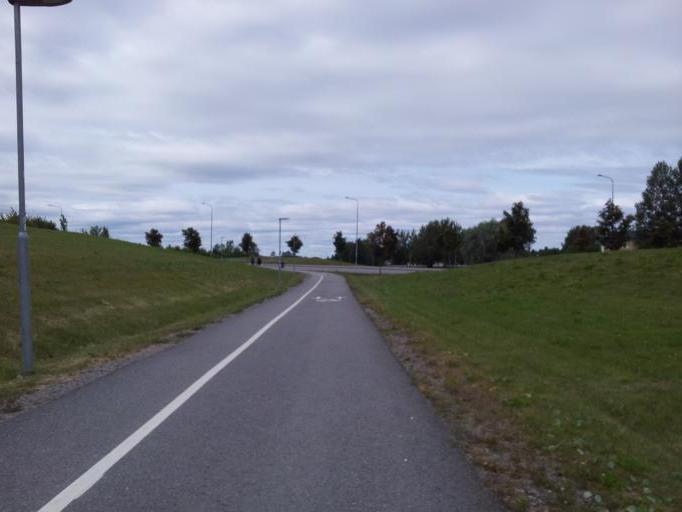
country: SE
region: Uppsala
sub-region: Uppsala Kommun
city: Gamla Uppsala
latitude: 59.8850
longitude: 17.6572
